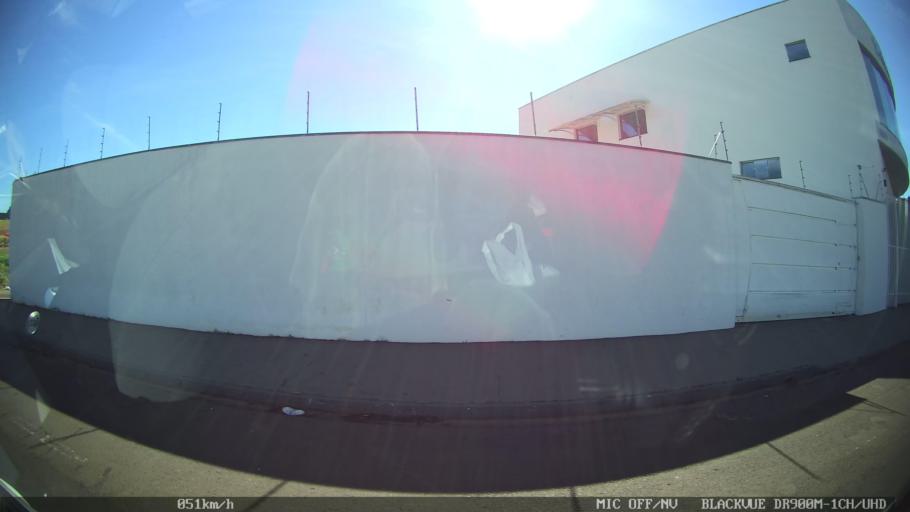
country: BR
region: Sao Paulo
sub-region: Franca
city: Franca
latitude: -20.5204
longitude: -47.3757
